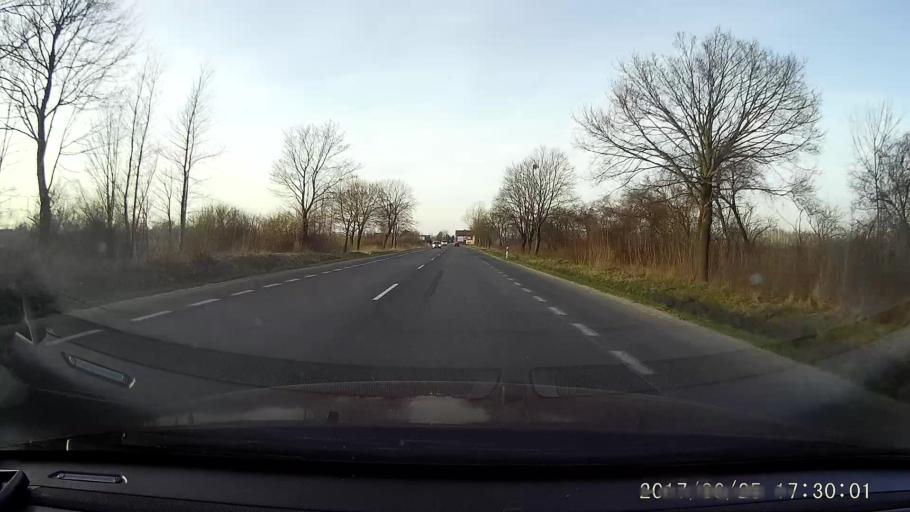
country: PL
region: Lower Silesian Voivodeship
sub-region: Powiat zgorzelecki
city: Sulikow
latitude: 51.0884
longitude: 15.0231
